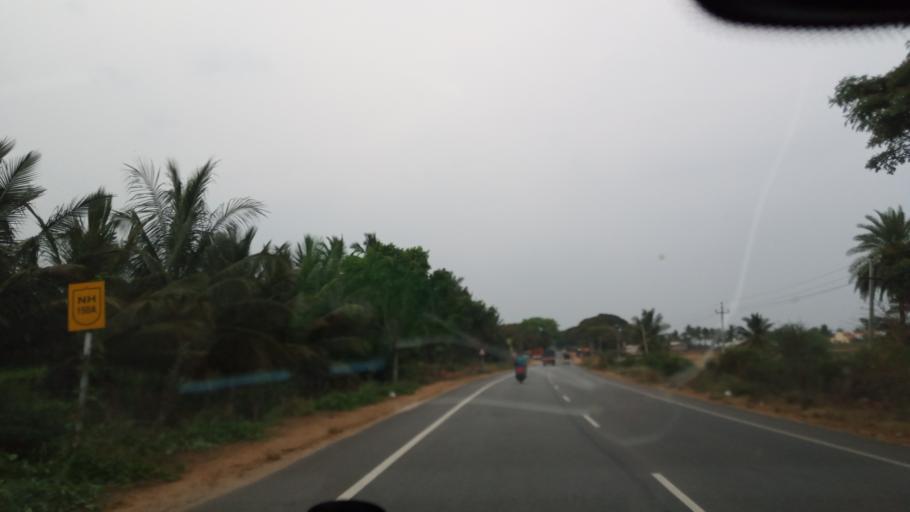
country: IN
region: Karnataka
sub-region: Mandya
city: Nagamangala
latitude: 12.7867
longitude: 76.7487
